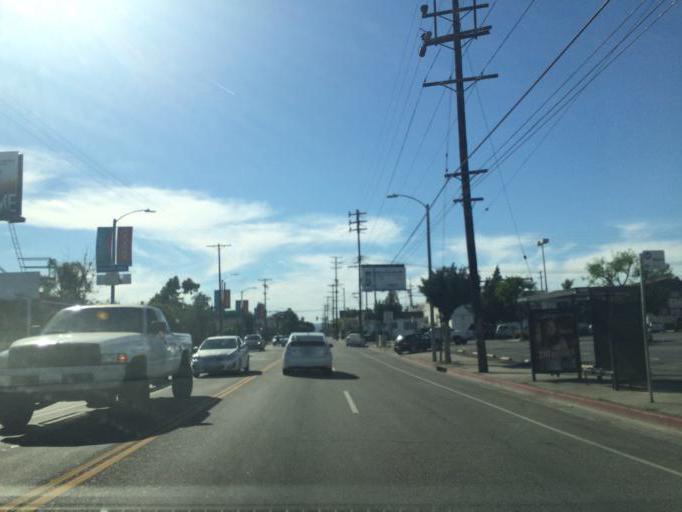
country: US
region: California
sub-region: Los Angeles County
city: Hollywood
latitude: 34.0835
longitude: -118.3268
